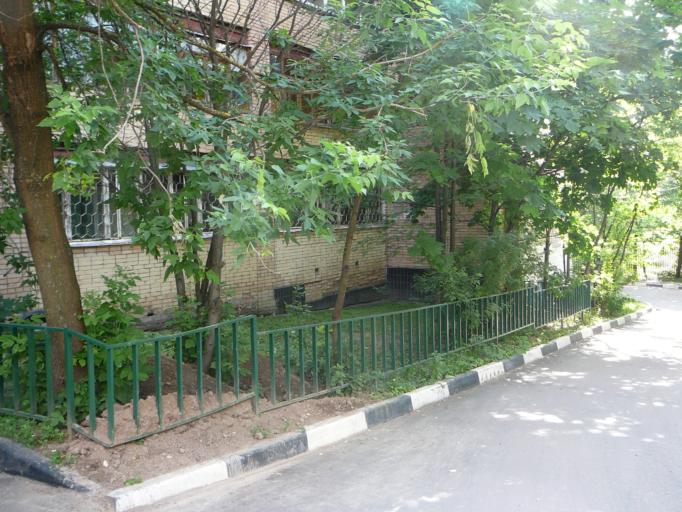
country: RU
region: Moskovskaya
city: Krasnogorsk
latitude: 55.8160
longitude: 37.3147
